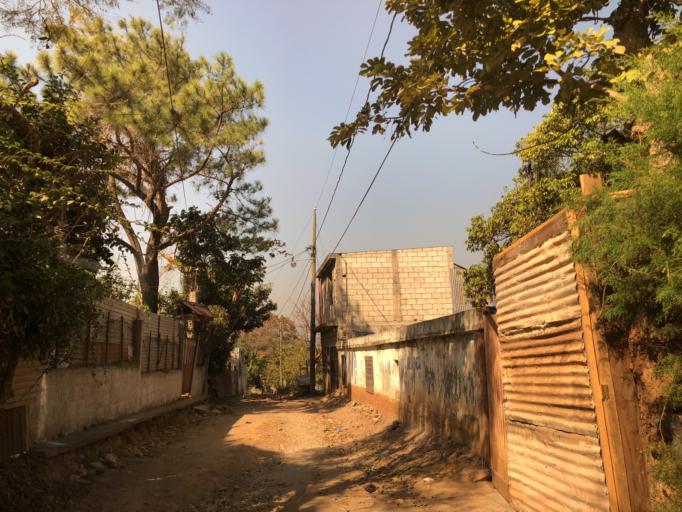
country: GT
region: Guatemala
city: Santa Catarina Pinula
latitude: 14.5396
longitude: -90.5171
